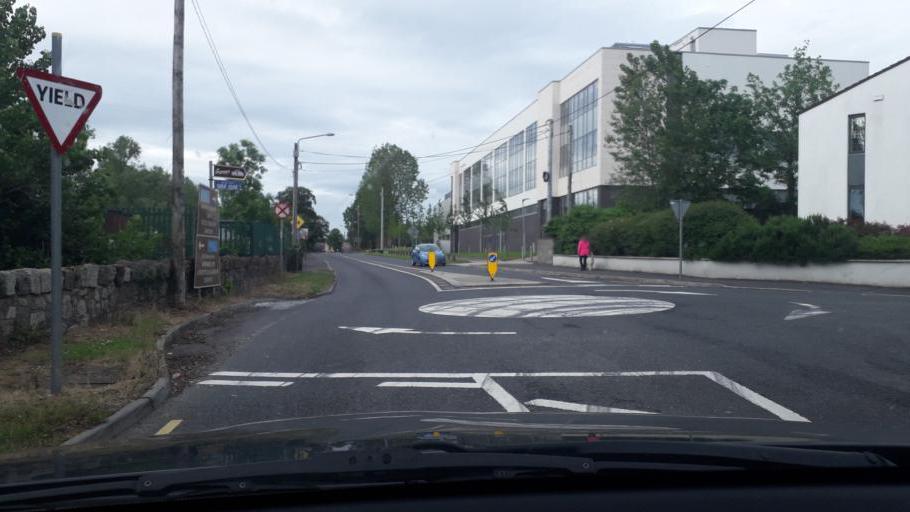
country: IE
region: Leinster
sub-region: County Carlow
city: Carlow
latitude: 52.8266
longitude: -6.9379
